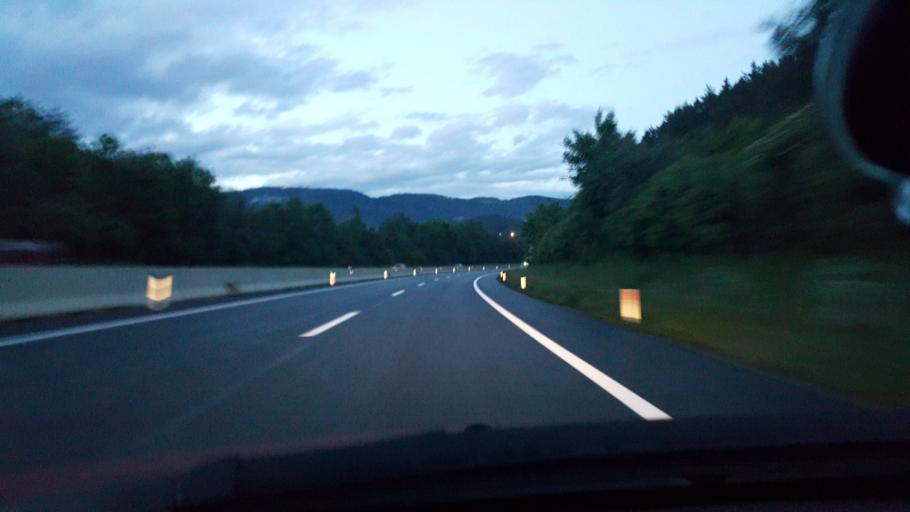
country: AT
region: Carinthia
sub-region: Politischer Bezirk Volkermarkt
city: Voelkermarkt
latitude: 46.6687
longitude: 14.5767
